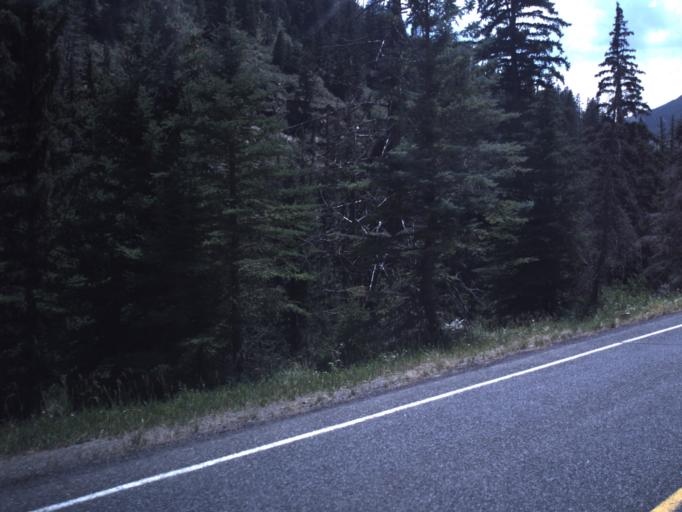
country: US
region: Utah
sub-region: Emery County
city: Huntington
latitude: 39.4896
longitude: -111.1578
